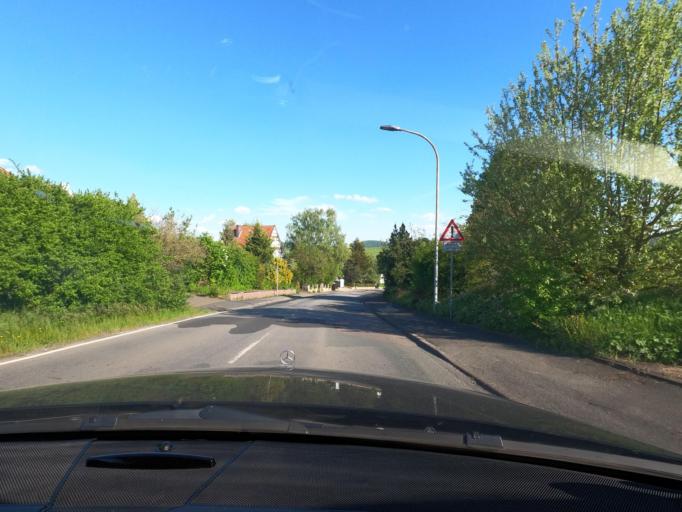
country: DE
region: Hesse
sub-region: Regierungsbezirk Kassel
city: Breuna
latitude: 51.3912
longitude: 9.1862
